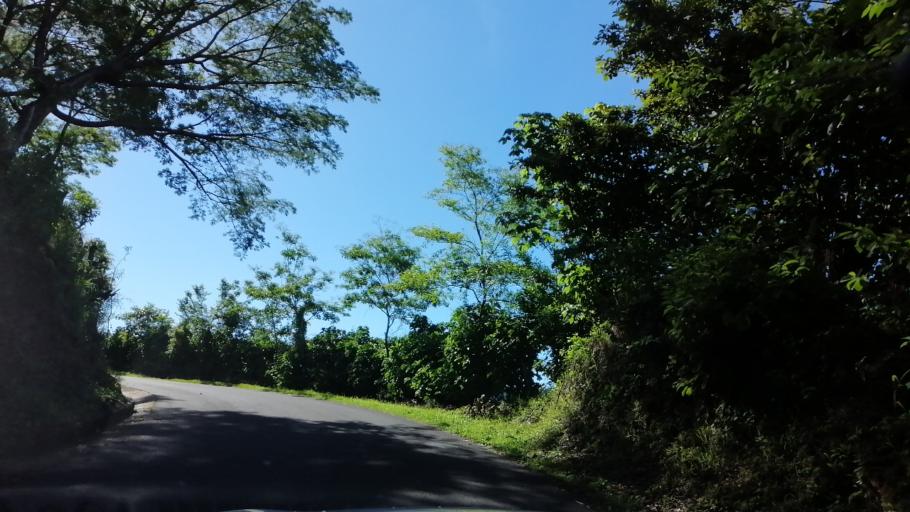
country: SV
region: Morazan
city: Corinto
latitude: 13.7977
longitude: -88.0053
